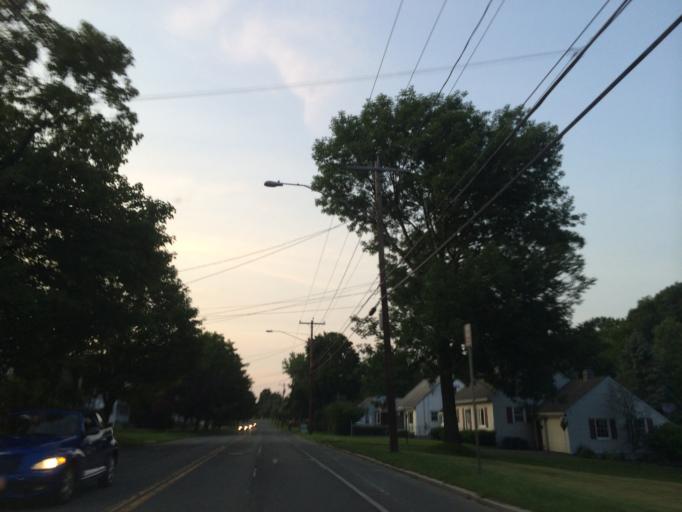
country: US
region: Massachusetts
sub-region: Berkshire County
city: Pittsfield
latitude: 42.4690
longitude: -73.2452
